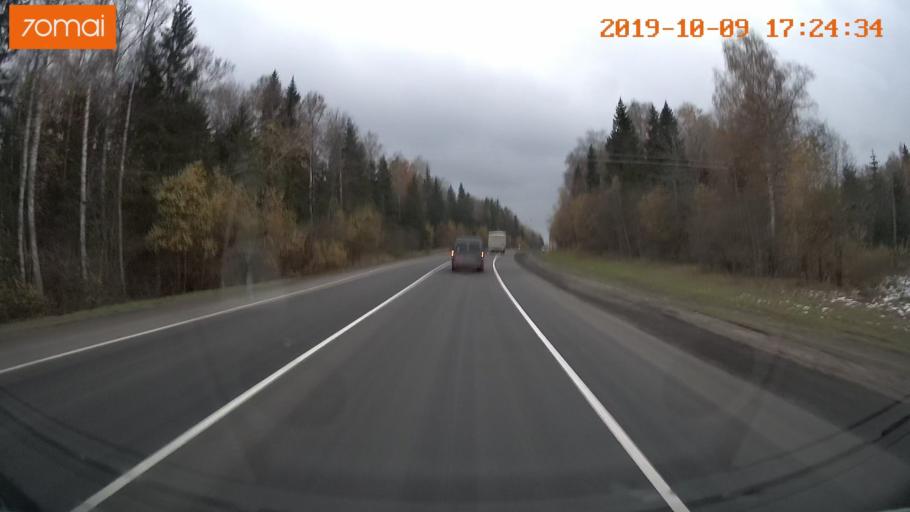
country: RU
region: Ivanovo
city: Furmanov
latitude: 57.1844
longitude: 41.1054
